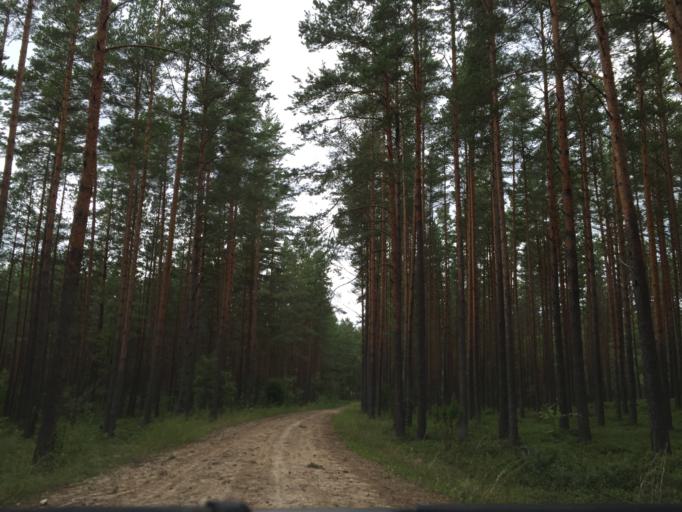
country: LV
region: Saulkrastu
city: Saulkrasti
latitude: 57.2185
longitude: 24.4149
